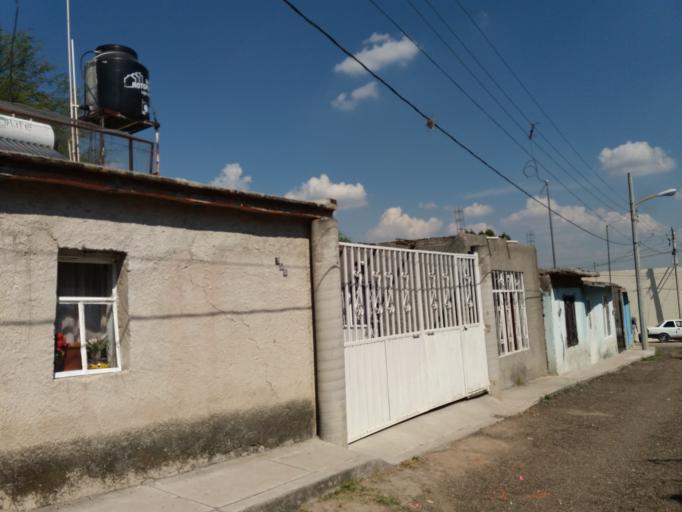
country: MX
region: Aguascalientes
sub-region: Aguascalientes
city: Penuelas (El Cienegal)
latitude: 21.7569
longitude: -102.3015
